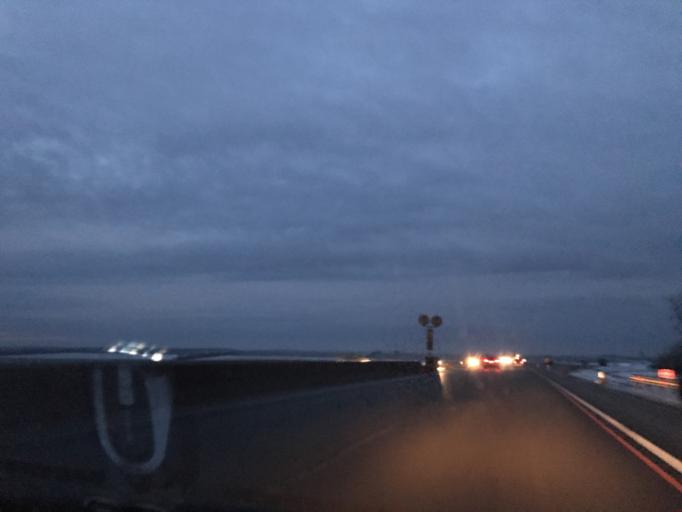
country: RU
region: Rostov
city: Samarskoye
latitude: 47.0174
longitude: 39.7353
